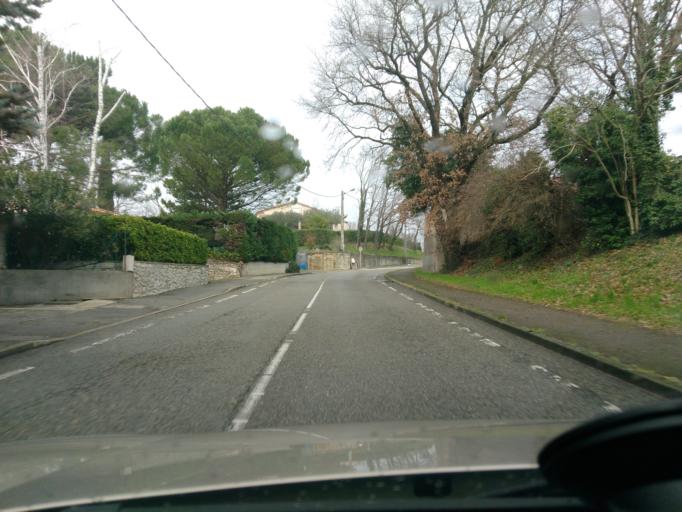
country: FR
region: Rhone-Alpes
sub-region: Departement de la Drome
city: Montelimar
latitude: 44.5761
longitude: 4.7628
